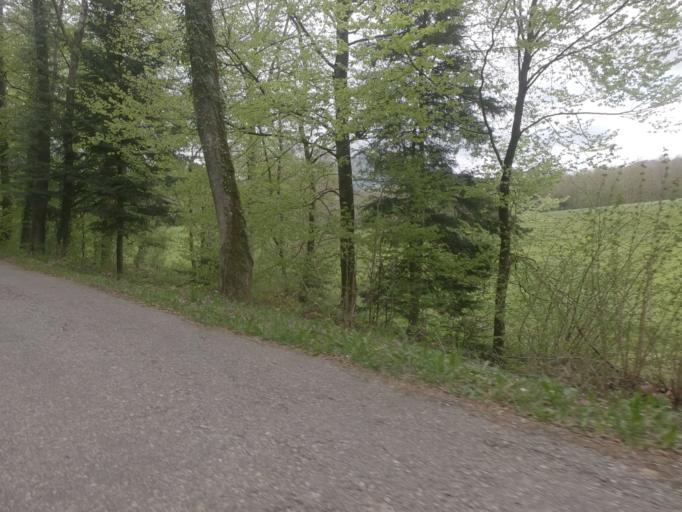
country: CH
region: Solothurn
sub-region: Bezirk Lebern
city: Riedholz
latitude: 47.2390
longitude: 7.5761
